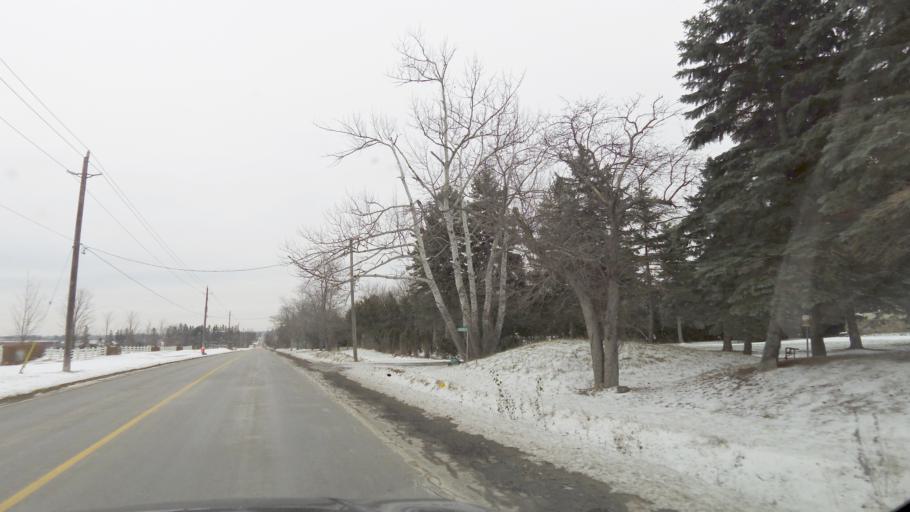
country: CA
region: Ontario
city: Vaughan
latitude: 43.8960
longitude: -79.5921
